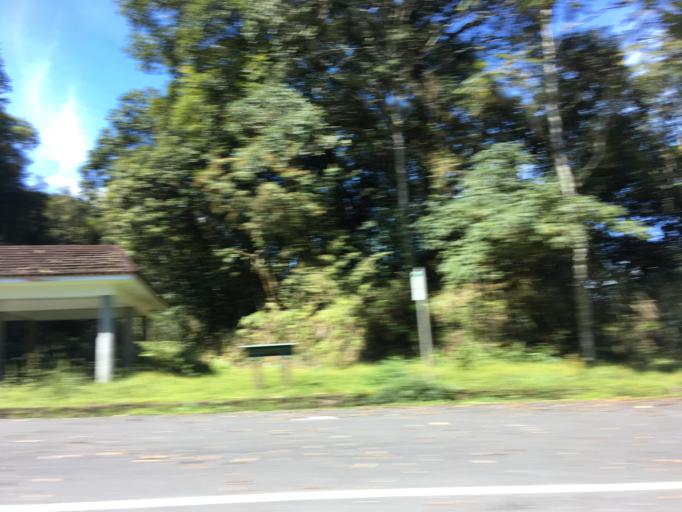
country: TW
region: Taiwan
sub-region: Yilan
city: Yilan
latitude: 24.5308
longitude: 121.5186
